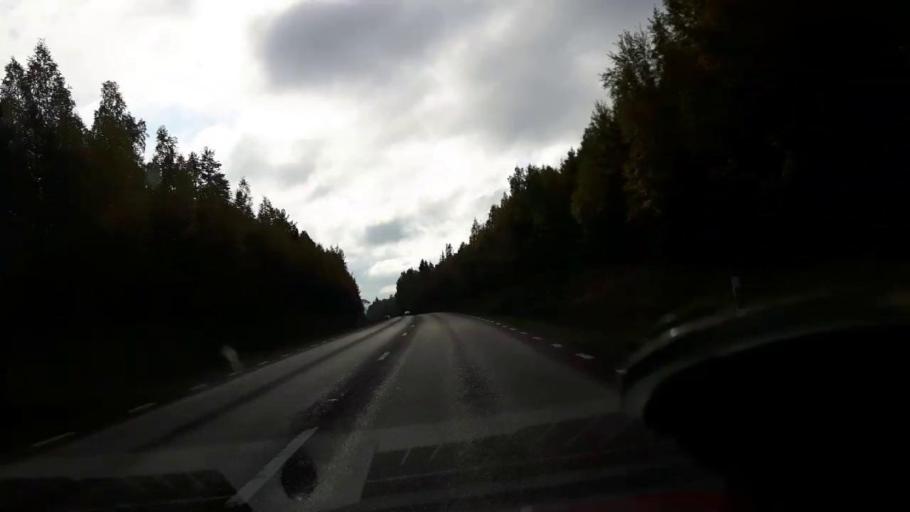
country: SE
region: Gaevleborg
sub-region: Ljusdals Kommun
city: Jaervsoe
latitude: 61.7400
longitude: 16.1593
